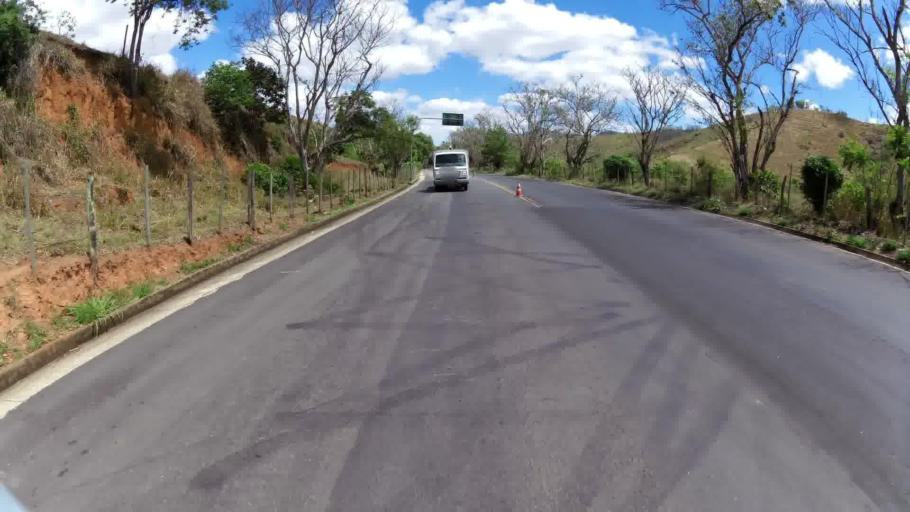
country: BR
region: Rio de Janeiro
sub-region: Itaperuna
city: Itaperuna
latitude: -21.3699
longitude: -41.9431
